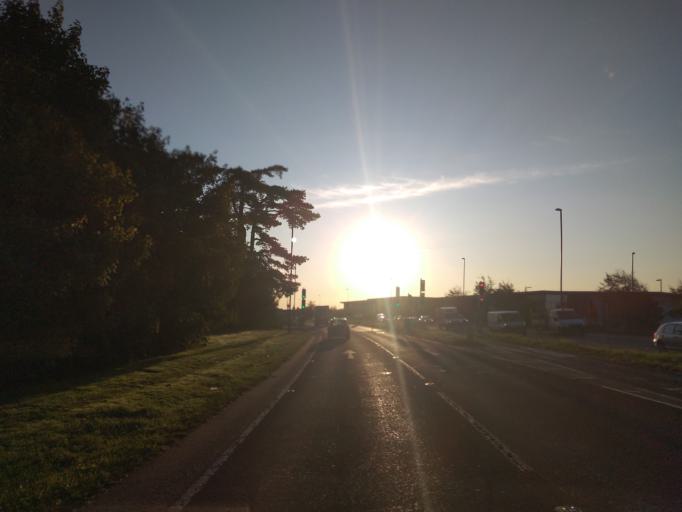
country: GB
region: England
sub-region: West Sussex
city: Rustington
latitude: 50.8187
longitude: -0.4980
